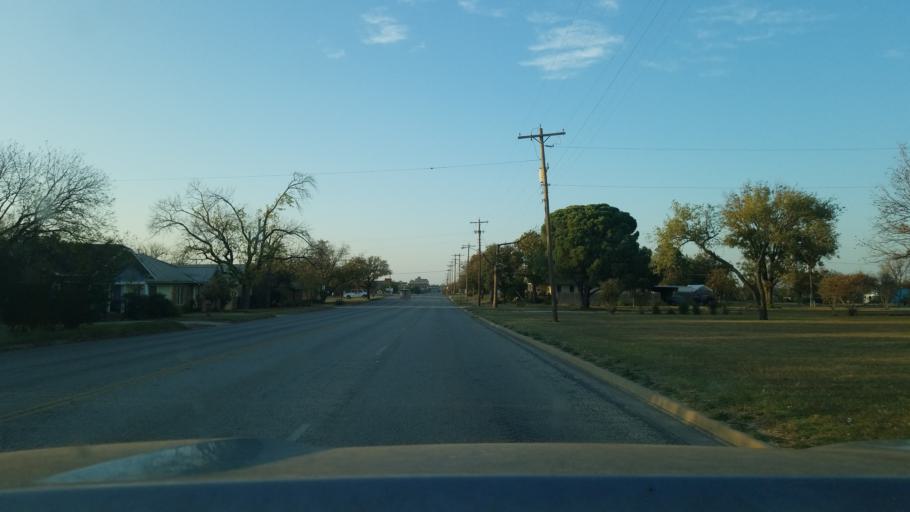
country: US
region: Texas
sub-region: Eastland County
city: Cisco
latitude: 32.3797
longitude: -98.9738
